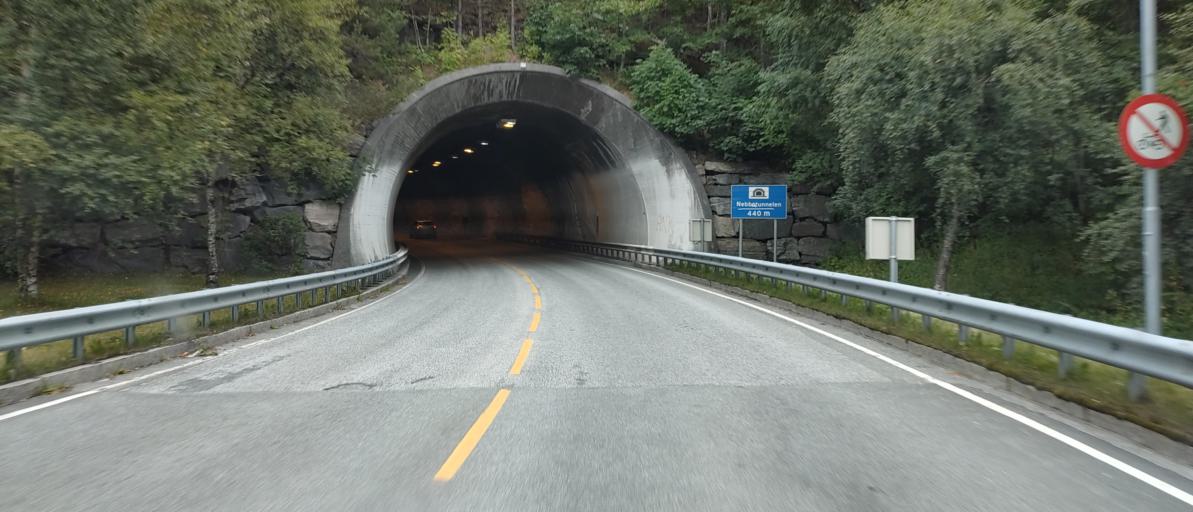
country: NO
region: More og Romsdal
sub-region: Rauma
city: Andalsnes
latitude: 62.5627
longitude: 7.6912
